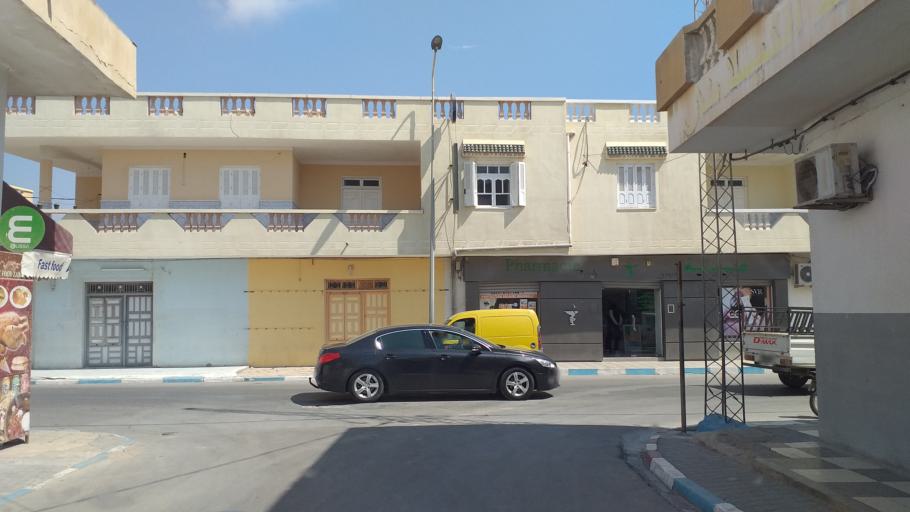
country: TN
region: Qabis
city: Gabes
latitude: 33.9410
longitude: 10.0665
